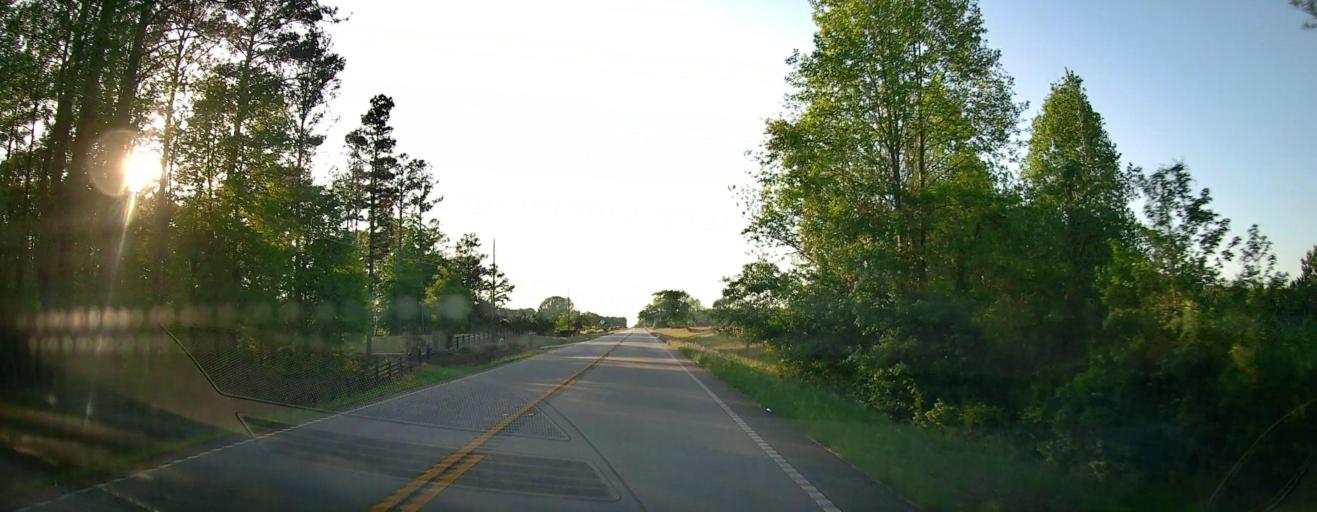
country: US
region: Georgia
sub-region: Walton County
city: Social Circle
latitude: 33.5560
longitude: -83.7452
